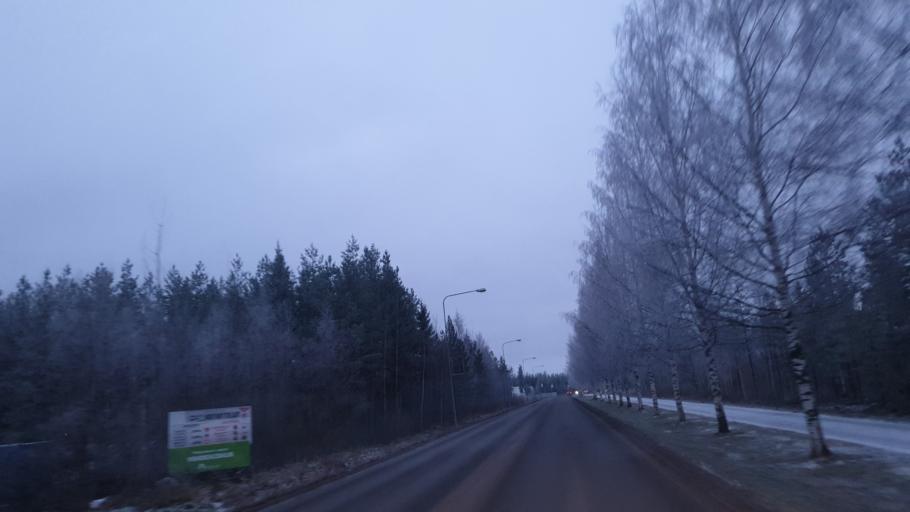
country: FI
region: Southern Ostrobothnia
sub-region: Seinaejoki
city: Nurmo
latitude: 62.7817
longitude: 22.8986
